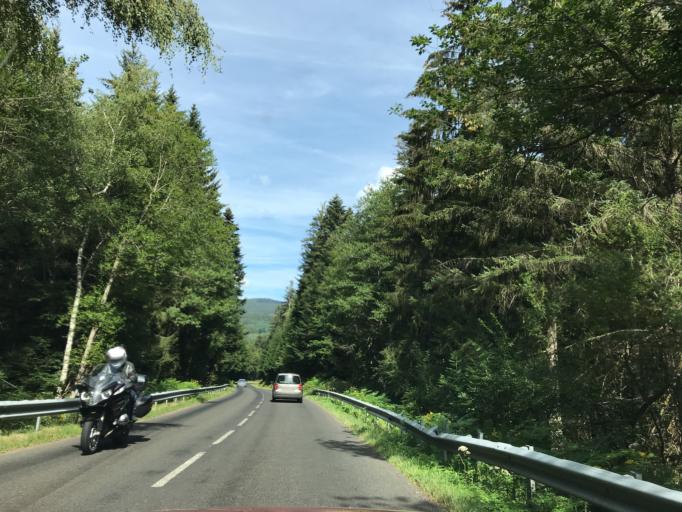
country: FR
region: Auvergne
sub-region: Departement du Puy-de-Dome
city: Celles-sur-Durolle
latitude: 45.7642
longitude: 3.6711
